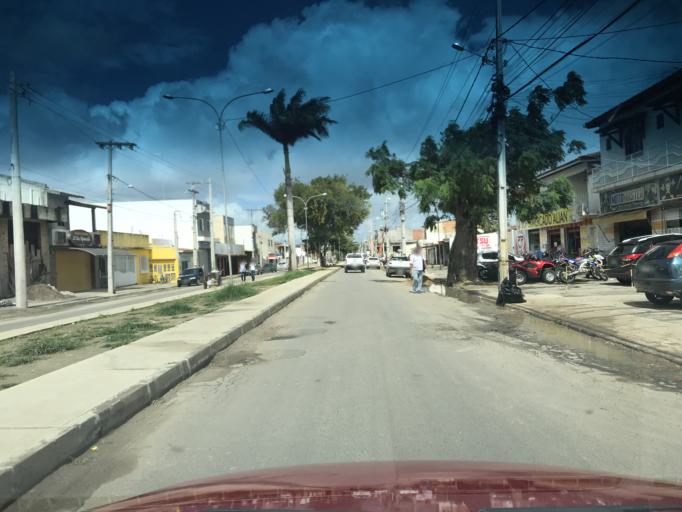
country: BR
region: Bahia
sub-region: Santo Antonio De Jesus
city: Santo Antonio de Jesus
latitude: -12.9734
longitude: -39.2733
